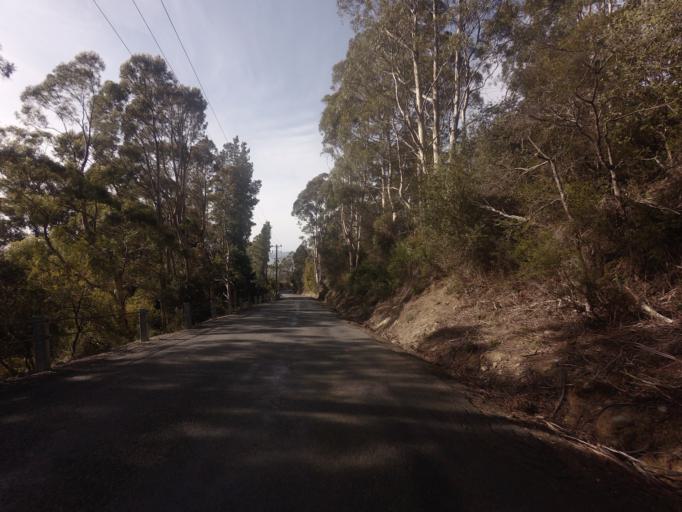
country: AU
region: Tasmania
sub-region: Kingborough
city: Kettering
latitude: -43.1669
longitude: 147.2112
